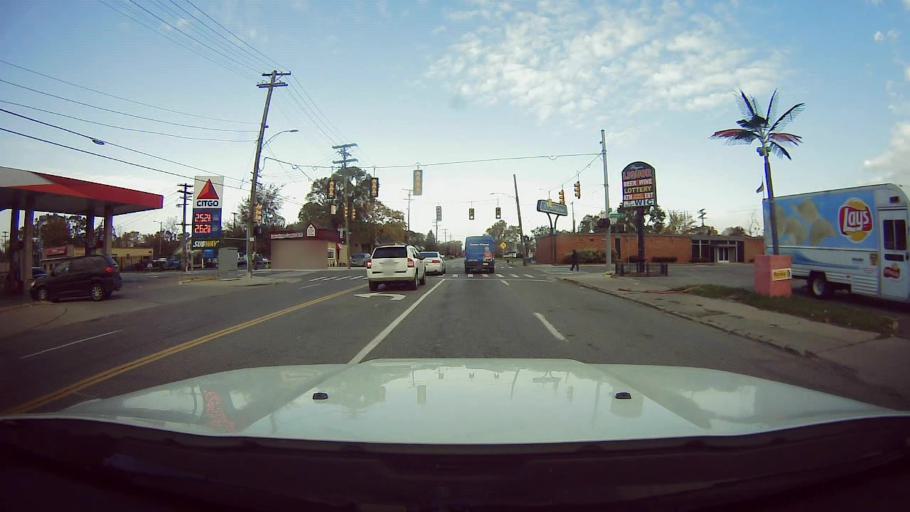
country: US
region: Michigan
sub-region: Wayne County
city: Dearborn
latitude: 42.3655
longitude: -83.1777
